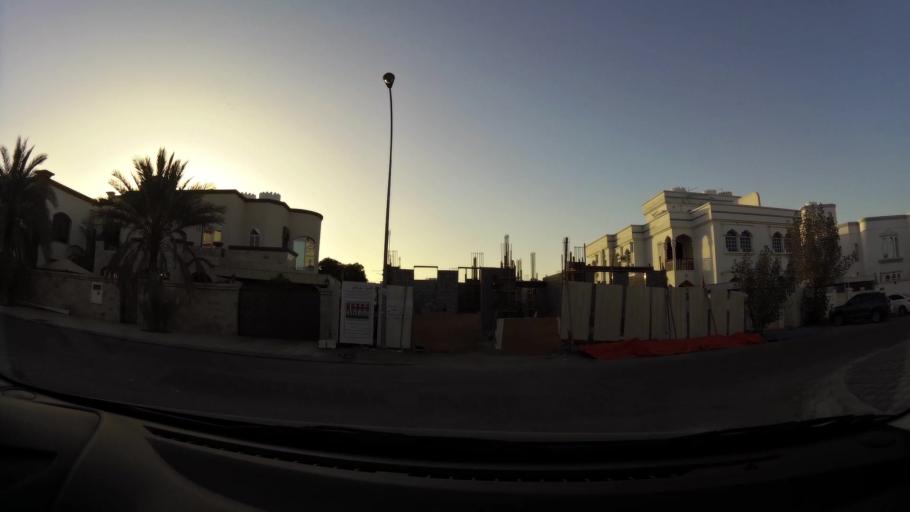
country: OM
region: Muhafazat Masqat
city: As Sib al Jadidah
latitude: 23.6063
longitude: 58.2285
